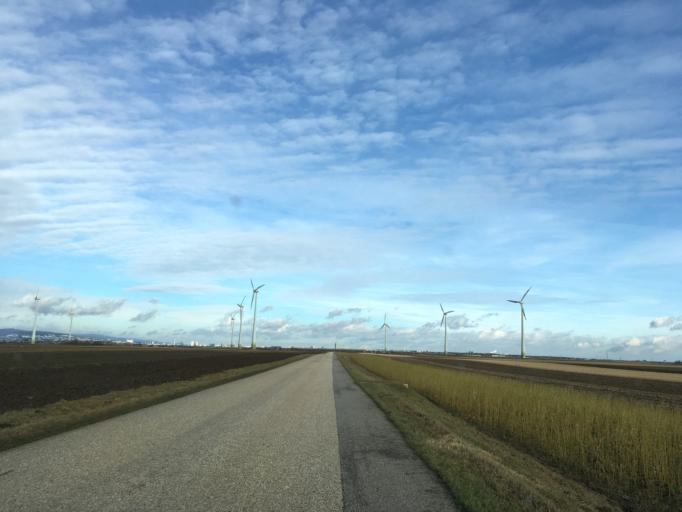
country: AT
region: Burgenland
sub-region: Politischer Bezirk Neusiedl am See
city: Pama
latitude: 48.0610
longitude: 17.0431
